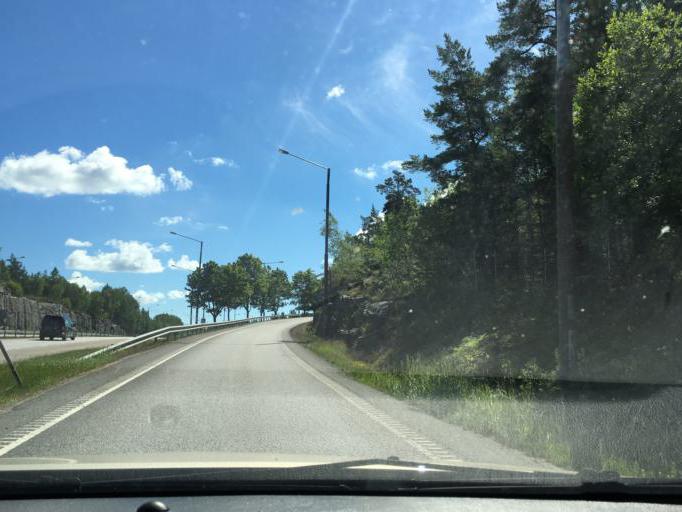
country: SE
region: Stockholm
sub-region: Nacka Kommun
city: Fisksatra
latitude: 59.2920
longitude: 18.2396
